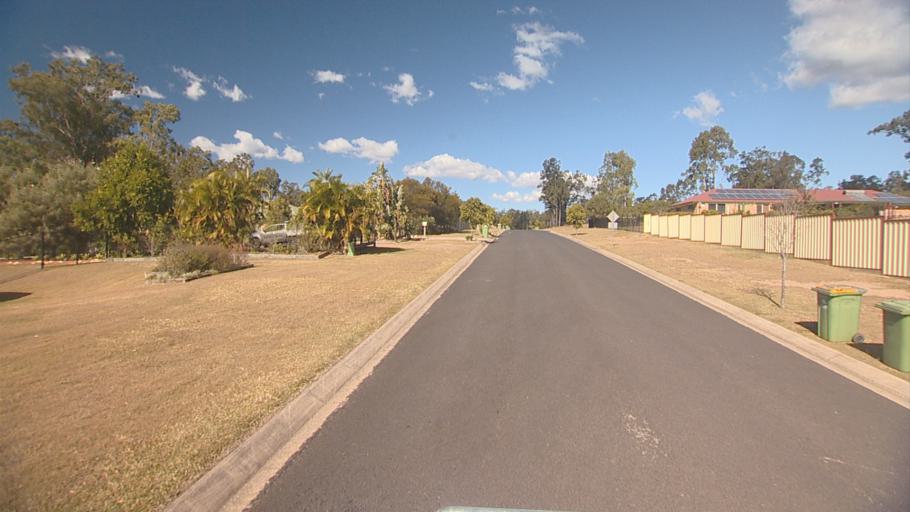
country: AU
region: Queensland
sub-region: Logan
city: North Maclean
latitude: -27.7498
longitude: 152.9401
